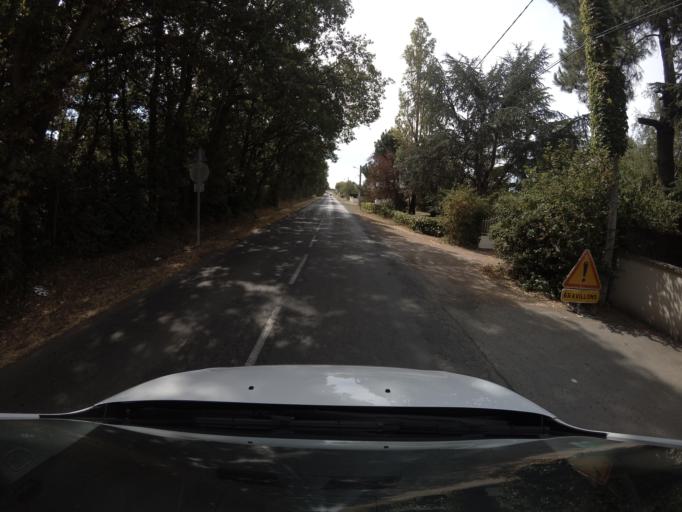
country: FR
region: Poitou-Charentes
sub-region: Departement des Deux-Sevres
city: Saint-Leger-de-Montbrun
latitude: 46.9935
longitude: -0.1295
